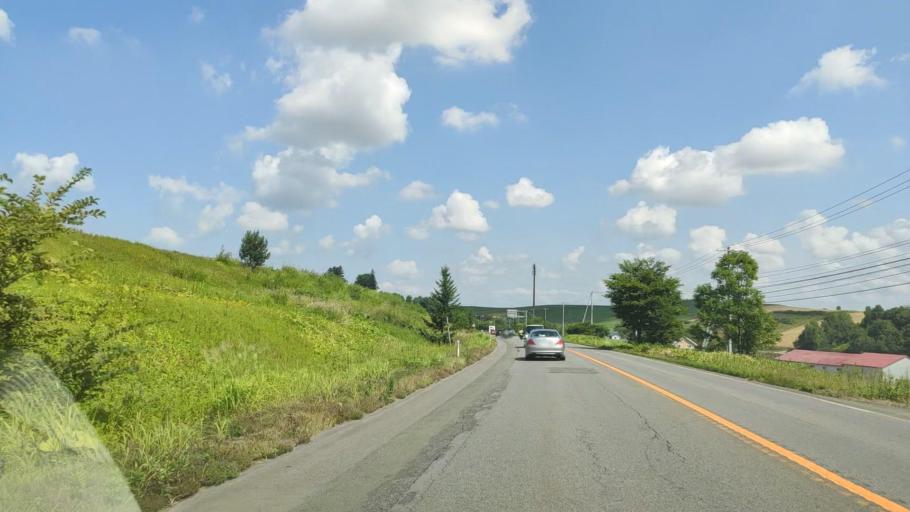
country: JP
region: Hokkaido
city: Shimo-furano
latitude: 43.5469
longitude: 142.4390
